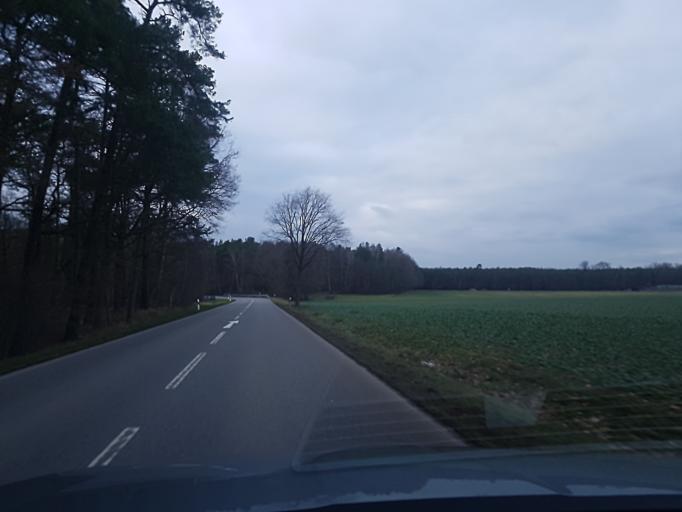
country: DE
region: Brandenburg
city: Finsterwalde
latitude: 51.6743
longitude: 13.6905
